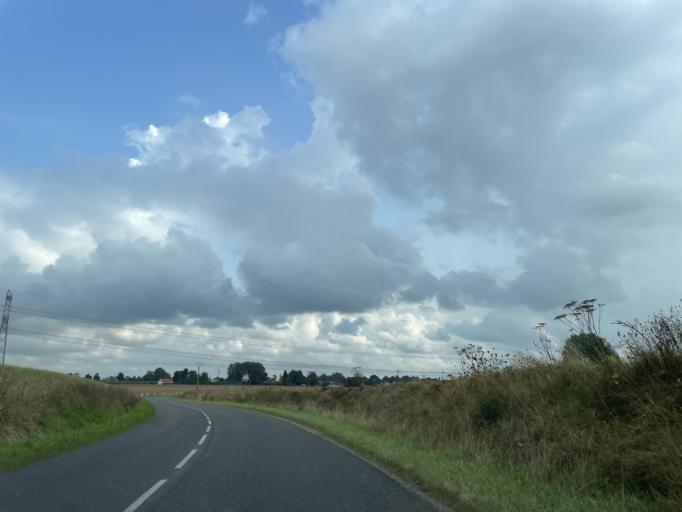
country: FR
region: Haute-Normandie
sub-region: Departement de la Seine-Maritime
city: Envermeu
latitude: 49.9378
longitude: 1.2700
